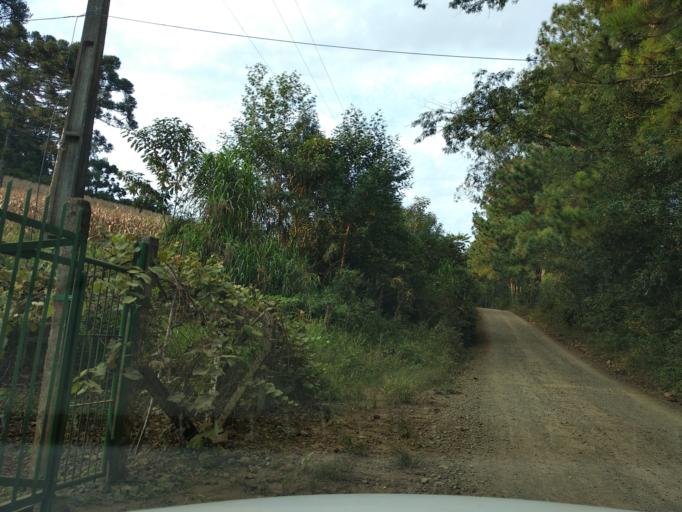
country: BR
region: Santa Catarina
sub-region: Videira
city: Videira
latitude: -26.9554
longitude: -51.1622
